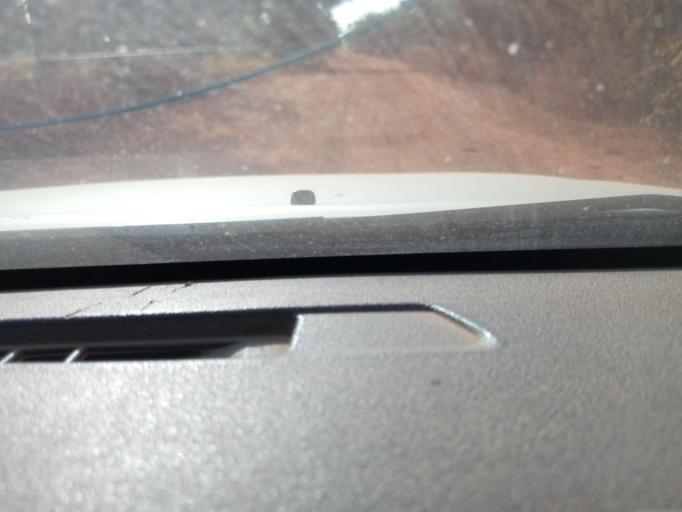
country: ML
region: Sikasso
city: Koutiala
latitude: 11.9619
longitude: -6.0931
